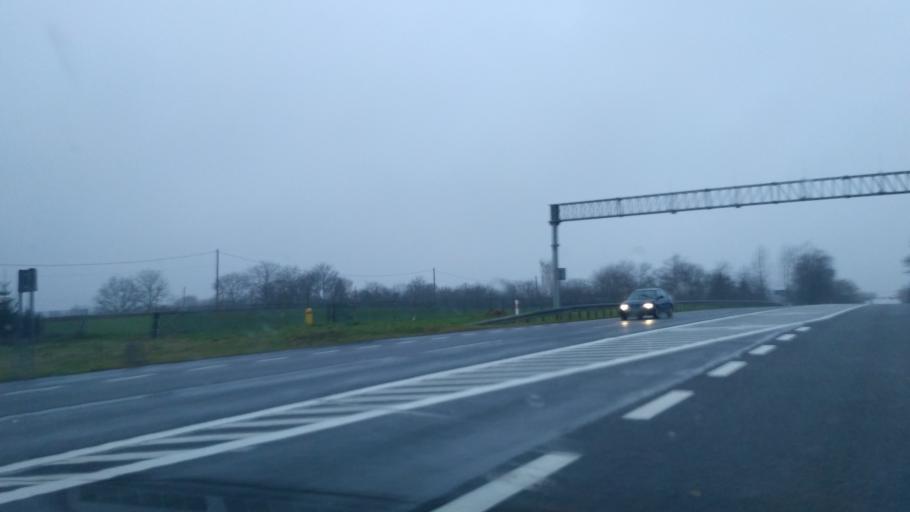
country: PL
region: Subcarpathian Voivodeship
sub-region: Powiat lancucki
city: Rogozno
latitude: 50.0679
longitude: 22.3794
